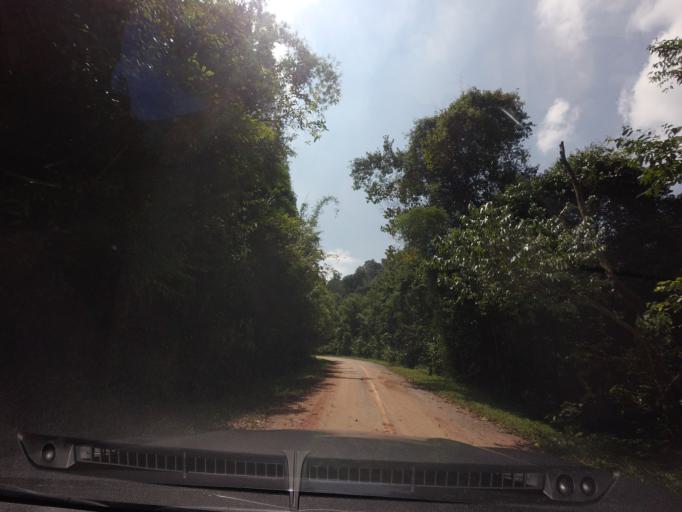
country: TH
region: Loei
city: Na Haeo
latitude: 17.5116
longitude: 100.9394
